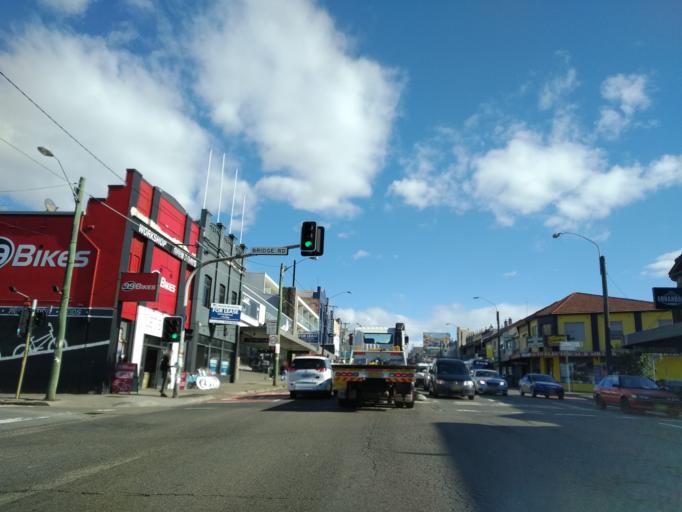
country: AU
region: New South Wales
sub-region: Marrickville
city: Camperdown
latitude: -33.8876
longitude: 151.1717
